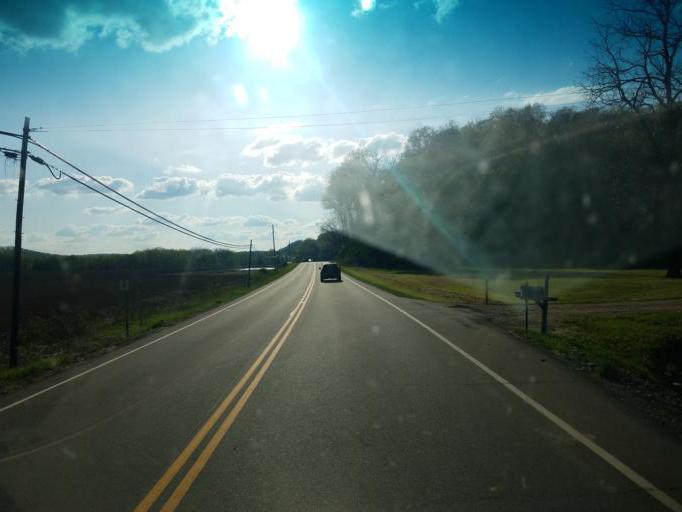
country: US
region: Ohio
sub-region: Coshocton County
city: Coshocton
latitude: 40.3416
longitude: -82.0281
